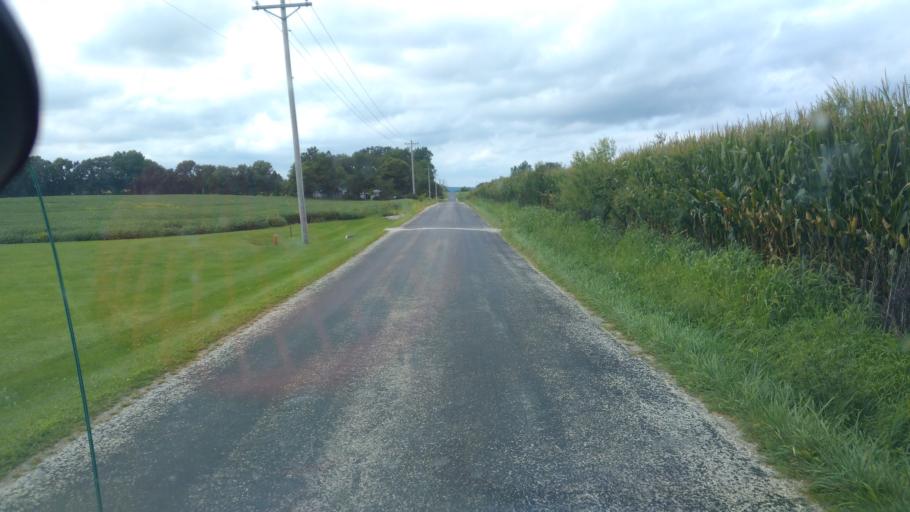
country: US
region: Ohio
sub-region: Ashland County
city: Ashland
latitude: 40.8219
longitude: -82.3633
